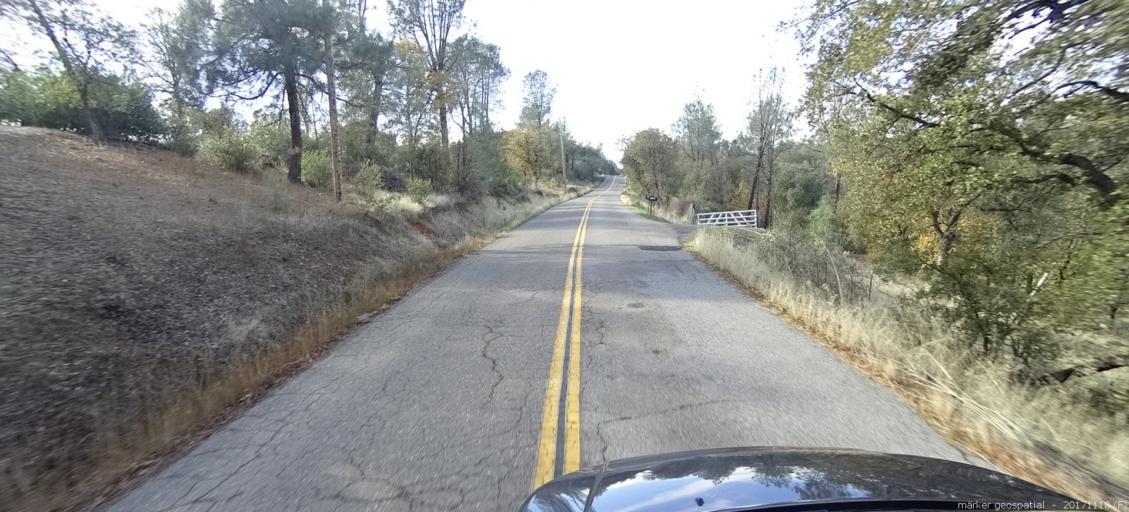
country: US
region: California
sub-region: Shasta County
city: Anderson
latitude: 40.4726
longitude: -122.4004
